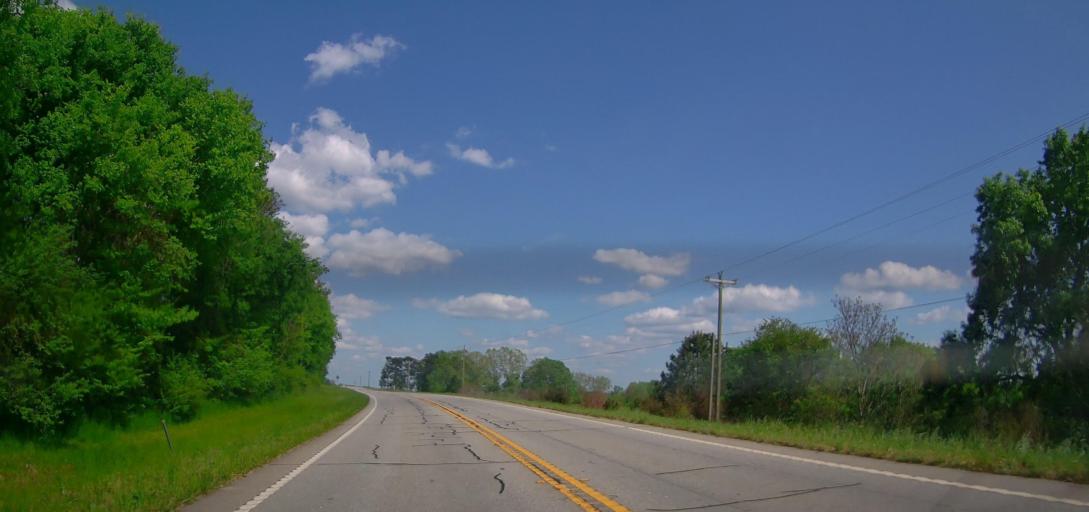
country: US
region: Georgia
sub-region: Greene County
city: Greensboro
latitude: 33.5971
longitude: -83.3004
